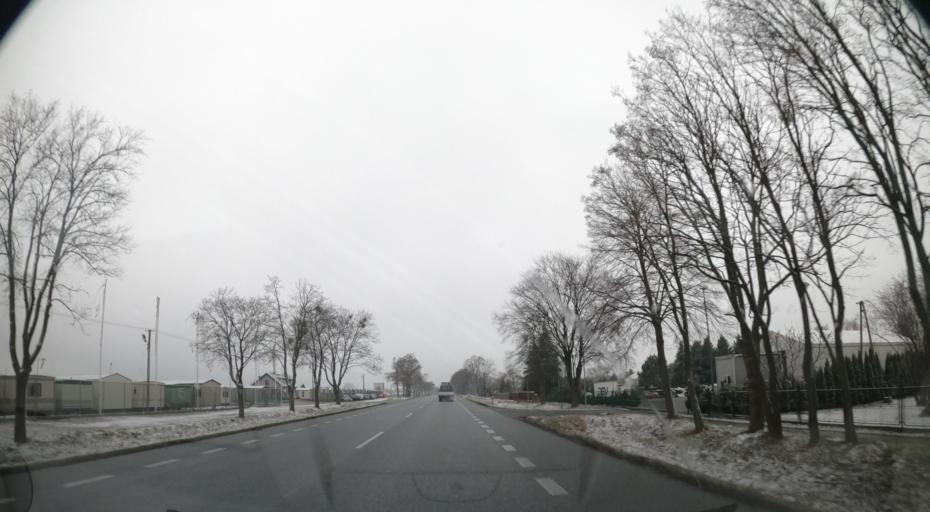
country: PL
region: Masovian Voivodeship
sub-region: Powiat sochaczewski
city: Teresin
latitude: 52.2140
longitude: 20.4077
